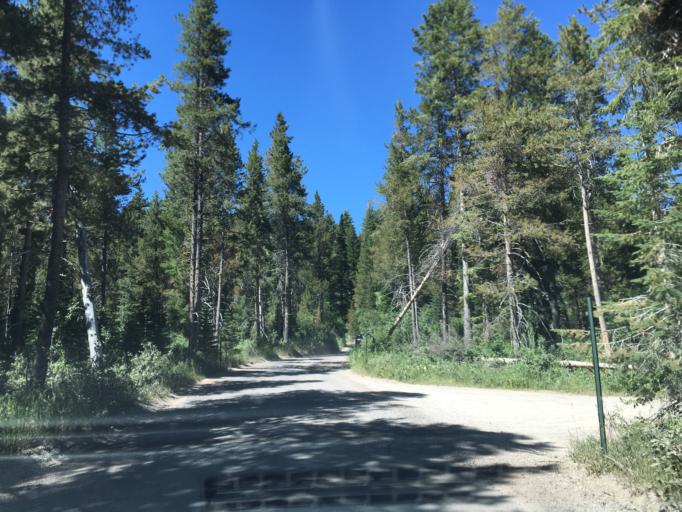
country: US
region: Wyoming
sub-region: Teton County
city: Moose Wilson Road
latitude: 43.6223
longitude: -110.7871
